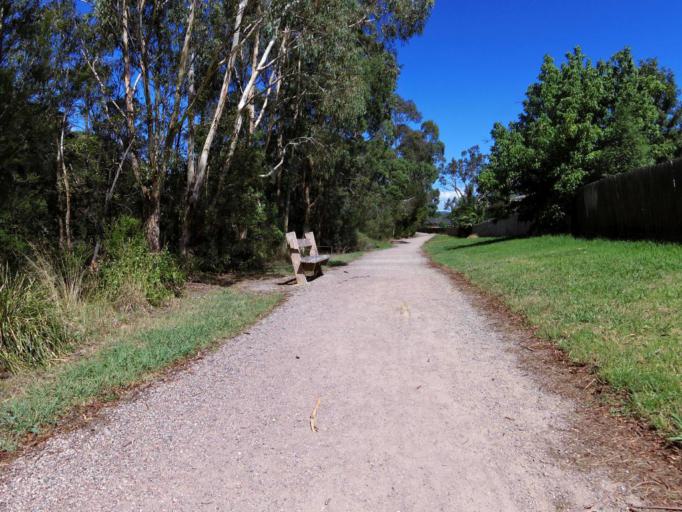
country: AU
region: Victoria
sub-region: Maroondah
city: Croydon North
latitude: -37.7725
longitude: 145.2998
